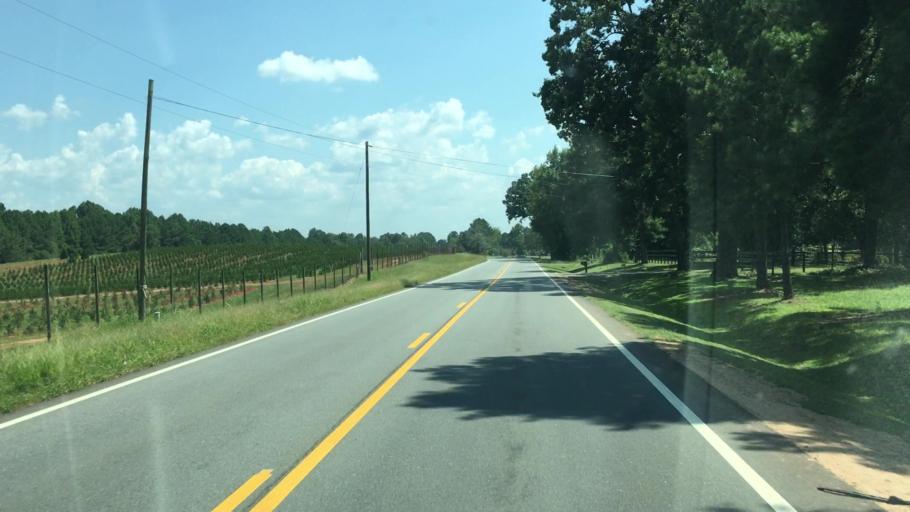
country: US
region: Georgia
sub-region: Oconee County
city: Watkinsville
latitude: 33.7470
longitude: -83.4332
